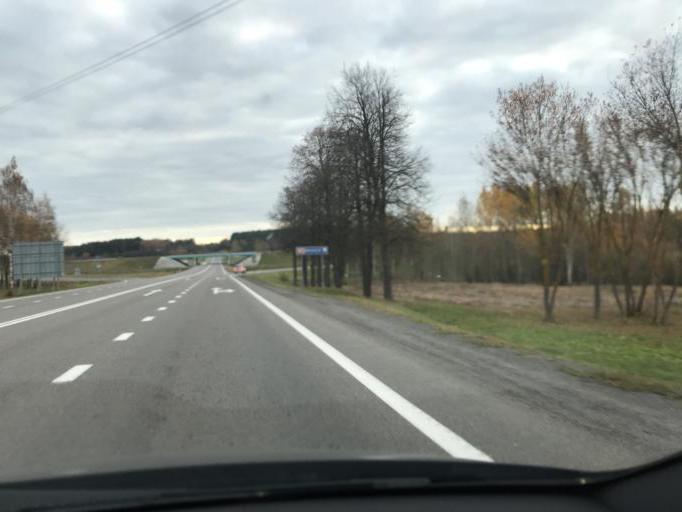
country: BY
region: Minsk
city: Astrashytski Haradok
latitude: 54.0547
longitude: 27.6976
